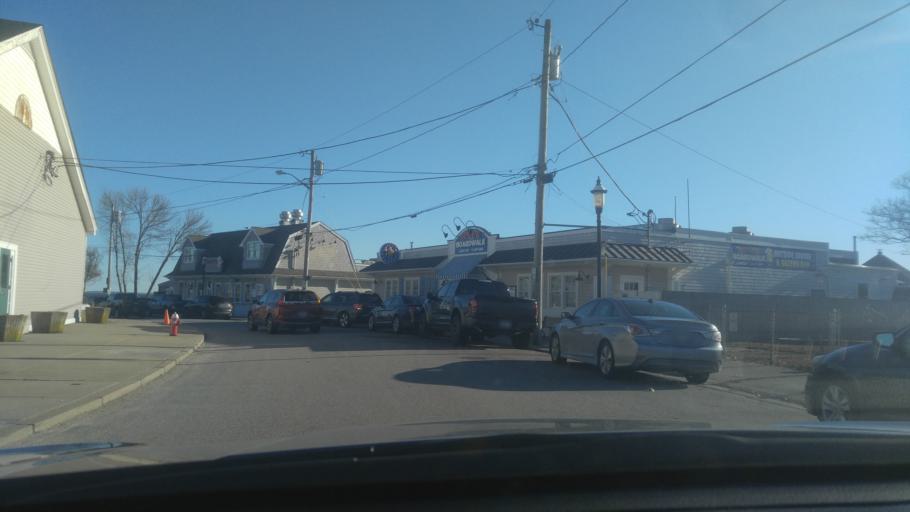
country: US
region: Rhode Island
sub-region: Kent County
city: Warwick
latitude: 41.6851
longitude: -71.3981
